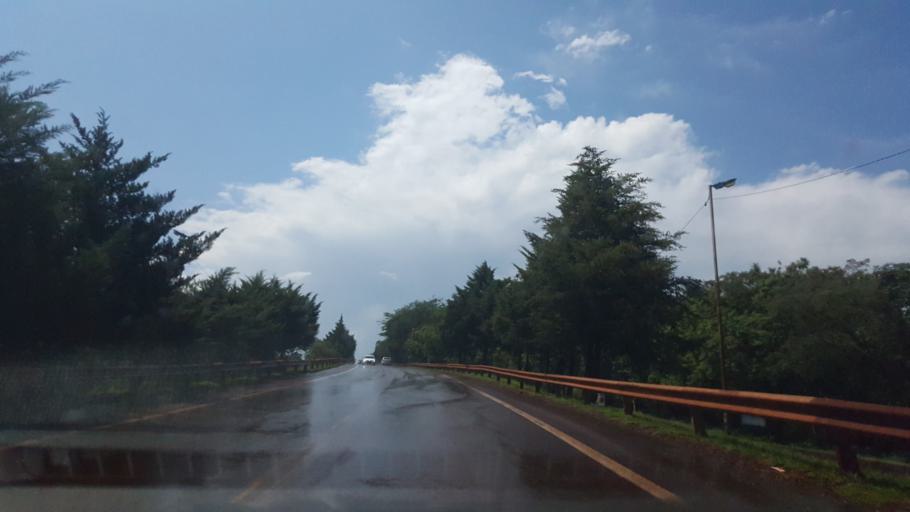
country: AR
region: Misiones
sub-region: Departamento de Eldorado
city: Eldorado
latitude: -26.4060
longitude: -54.6359
